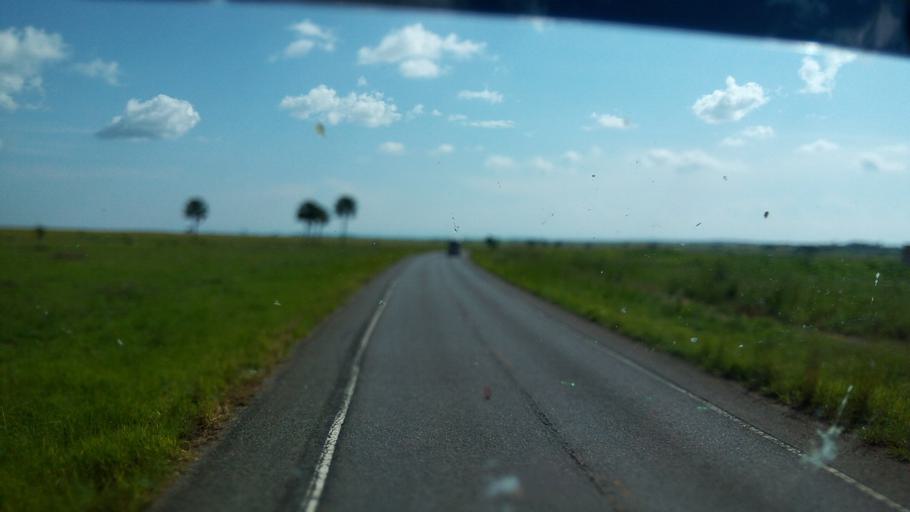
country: UG
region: Northern Region
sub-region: Nwoya District
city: Nwoya
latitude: 2.5631
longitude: 31.6540
